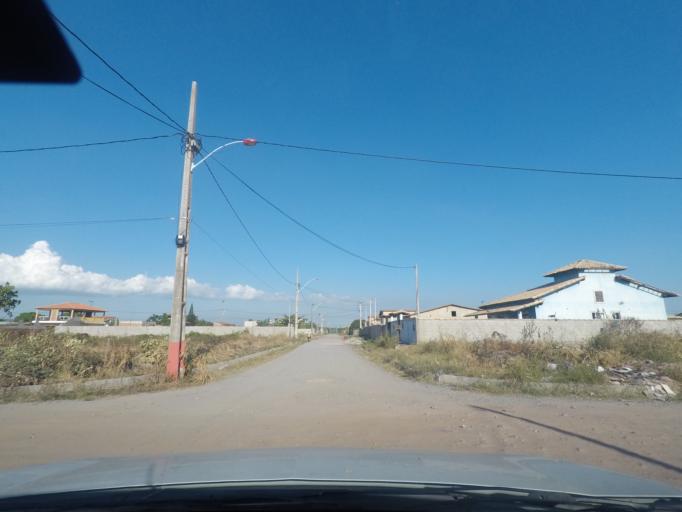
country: BR
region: Rio de Janeiro
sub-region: Marica
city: Marica
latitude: -22.9619
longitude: -42.9290
